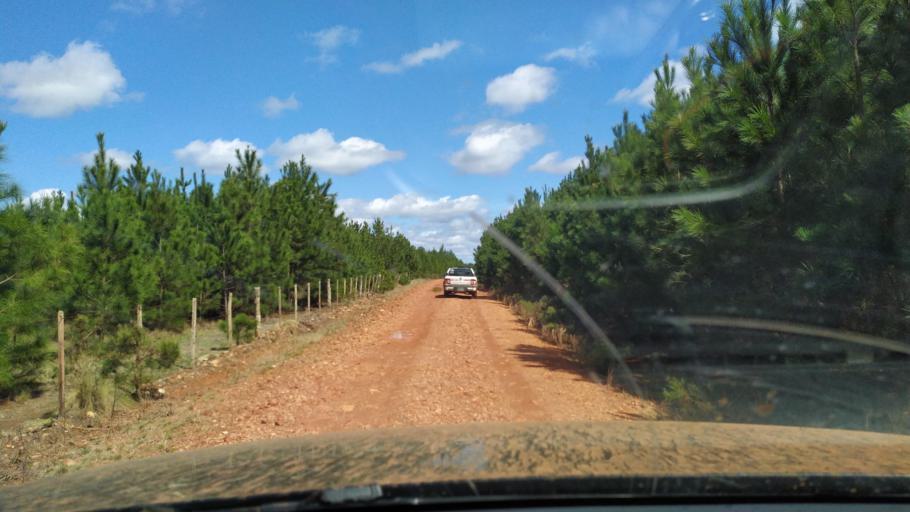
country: AR
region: Corrientes
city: Santo Tome
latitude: -28.4655
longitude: -55.9774
